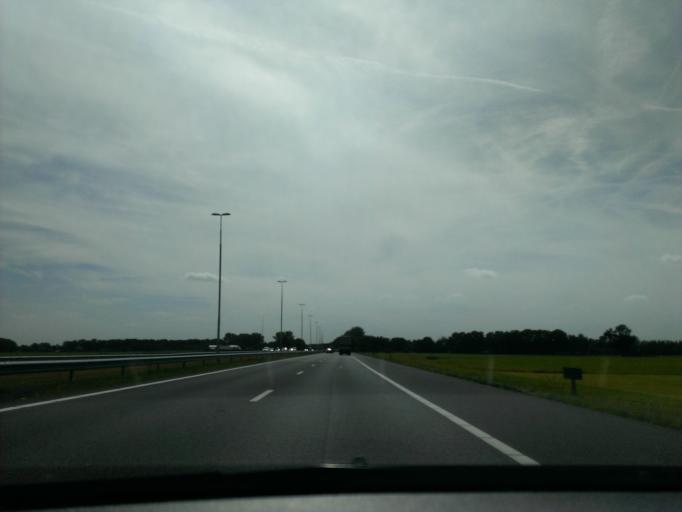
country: NL
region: Gelderland
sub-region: Gemeente Epe
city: Oene
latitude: 52.3556
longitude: 6.0228
